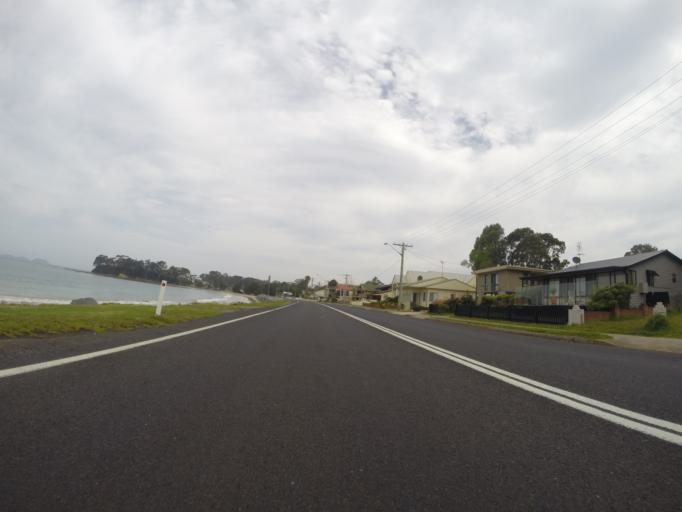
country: AU
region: New South Wales
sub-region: Eurobodalla
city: Batemans Bay
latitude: -35.7343
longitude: 150.2069
